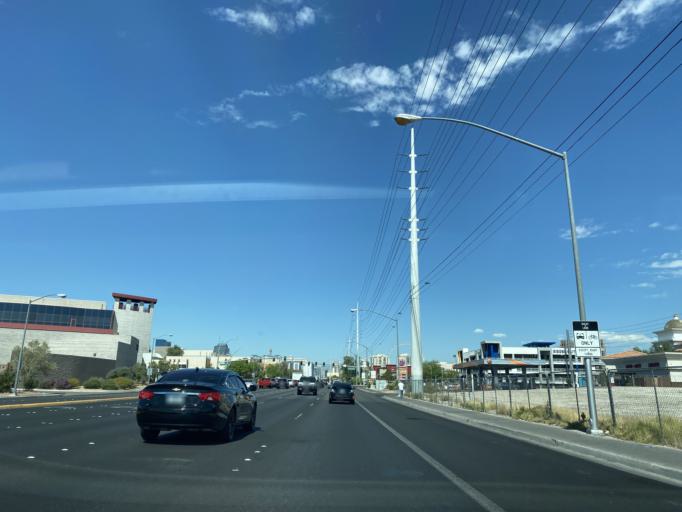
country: US
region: Nevada
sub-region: Clark County
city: Paradise
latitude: 36.1148
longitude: -115.1447
